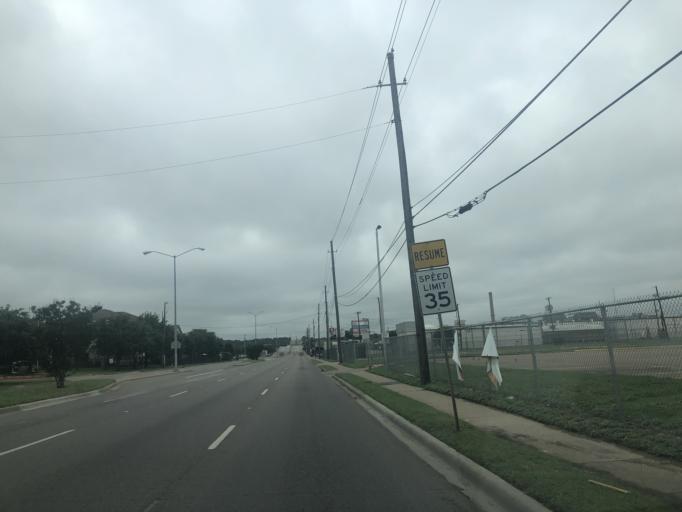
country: US
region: Texas
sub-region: Dallas County
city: Dallas
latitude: 32.7815
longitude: -96.8567
